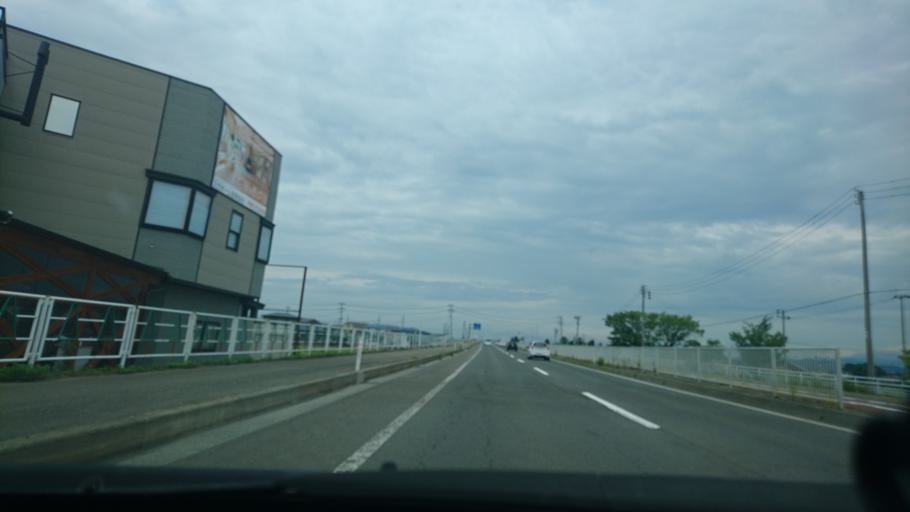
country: JP
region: Akita
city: Omagari
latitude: 39.4584
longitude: 140.4954
